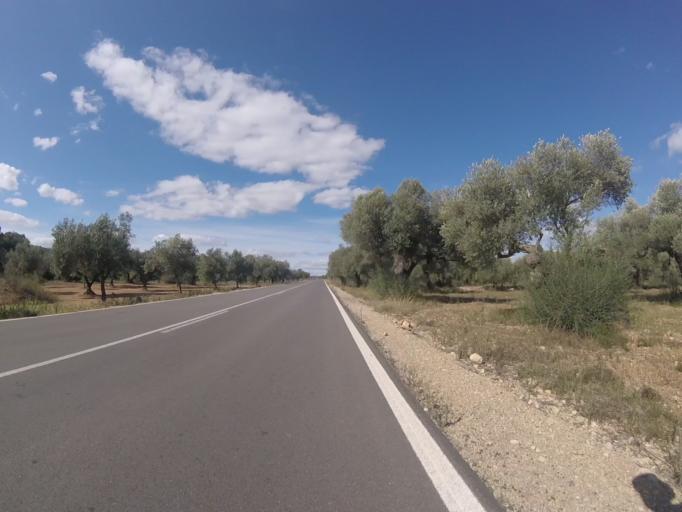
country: ES
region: Valencia
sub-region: Provincia de Castello
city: Chert/Xert
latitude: 40.4303
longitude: 0.1406
